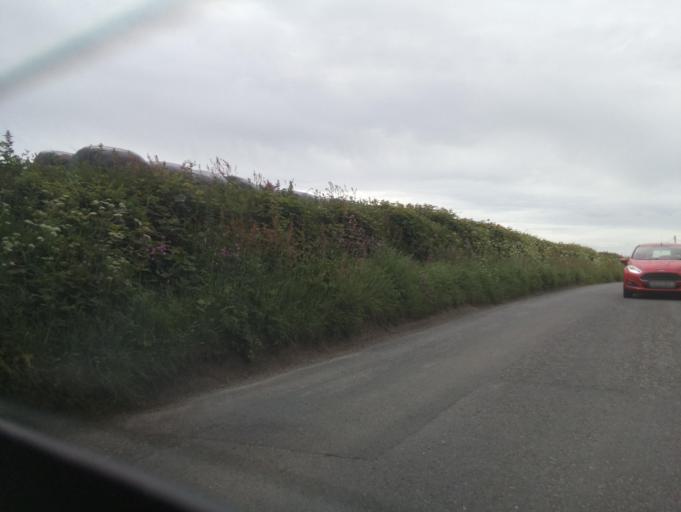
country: GB
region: England
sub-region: Devon
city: Dartmouth
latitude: 50.3520
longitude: -3.6609
